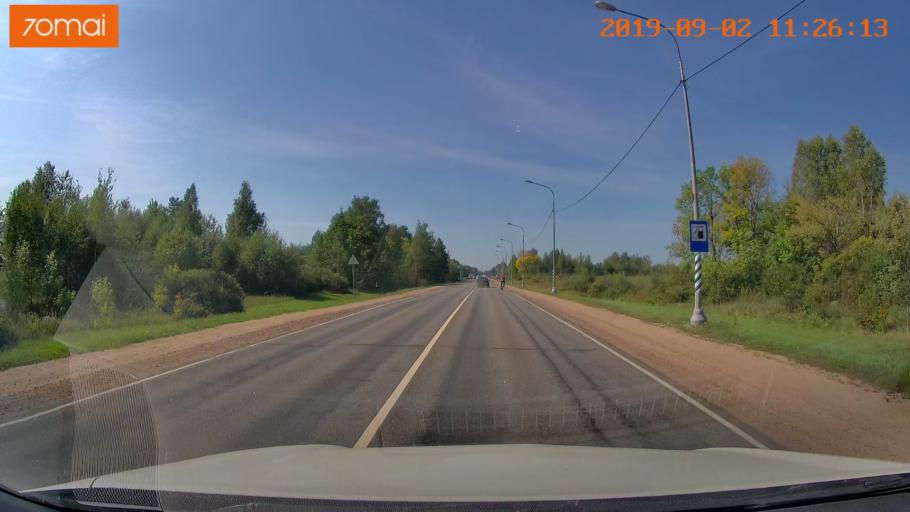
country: RU
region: Smolensk
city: Roslavl'
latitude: 53.9941
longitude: 32.9352
